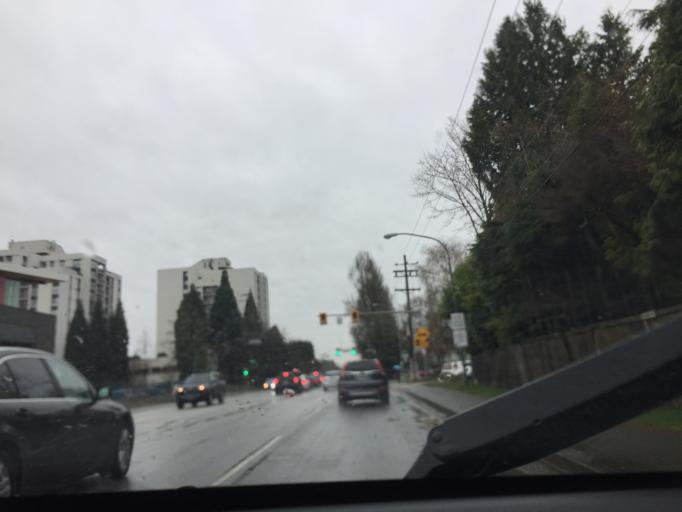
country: CA
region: British Columbia
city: Richmond
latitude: 49.1637
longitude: -123.1479
